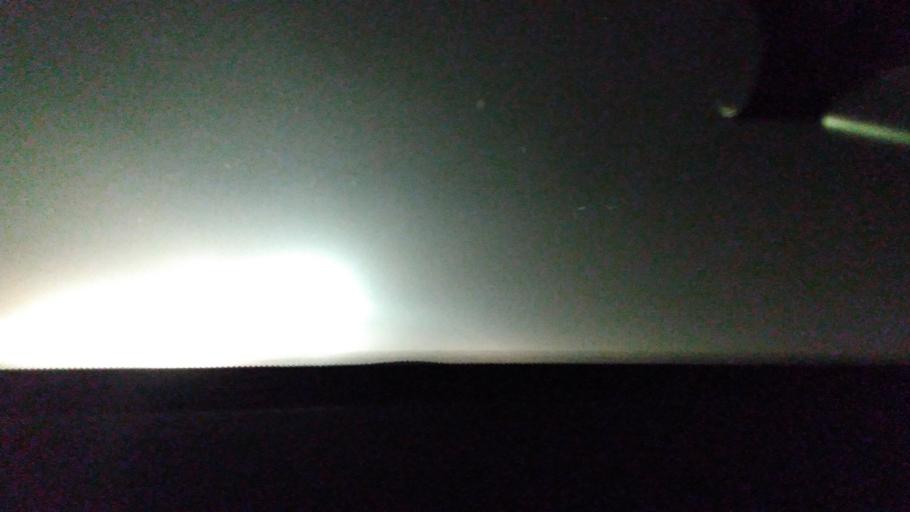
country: RU
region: Moskovskaya
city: Yegor'yevsk
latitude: 55.4231
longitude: 39.0380
